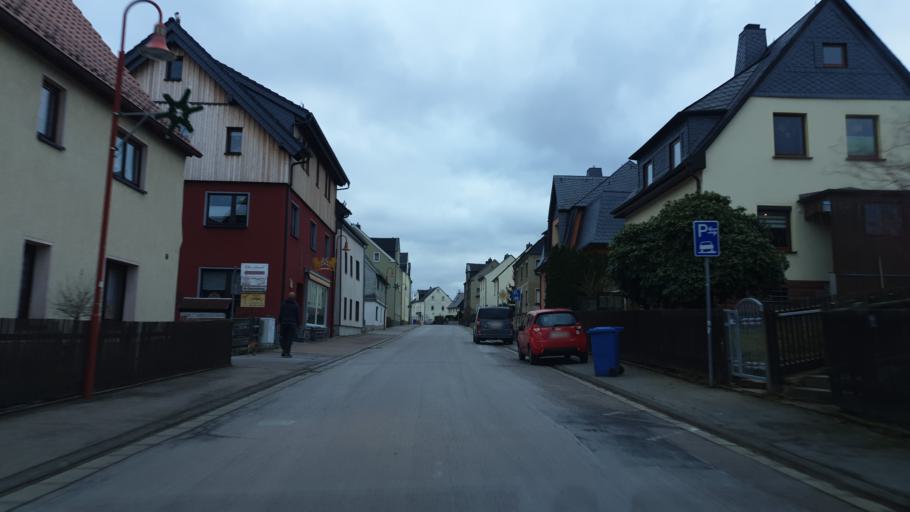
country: DE
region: Saxony
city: Hohndorf
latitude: 50.7391
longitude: 12.6609
